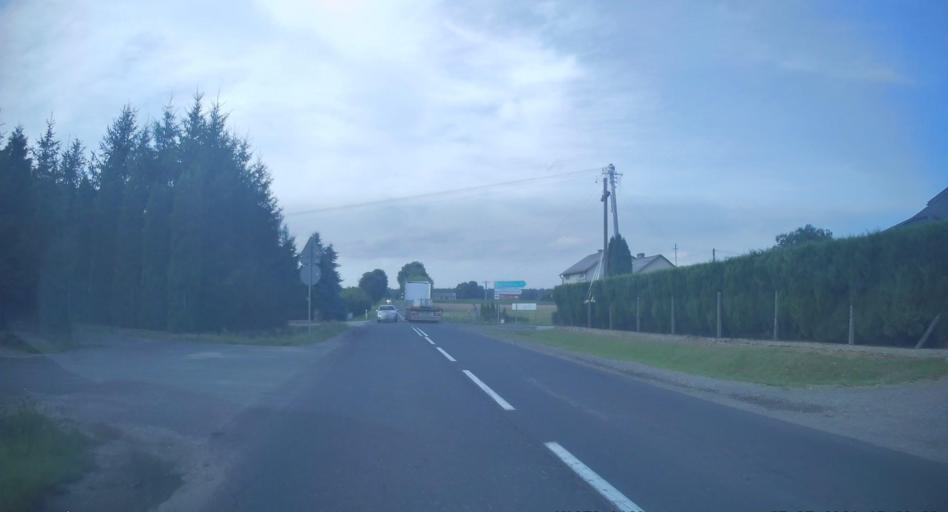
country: PL
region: Lodz Voivodeship
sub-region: Powiat tomaszowski
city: Rzeczyca
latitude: 51.6727
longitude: 20.2649
